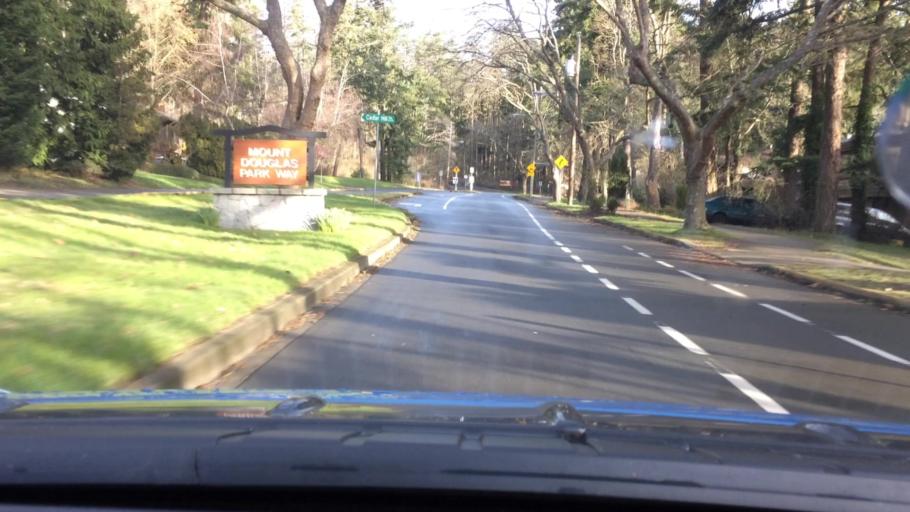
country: CA
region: British Columbia
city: Oak Bay
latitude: 48.4893
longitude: -123.3378
